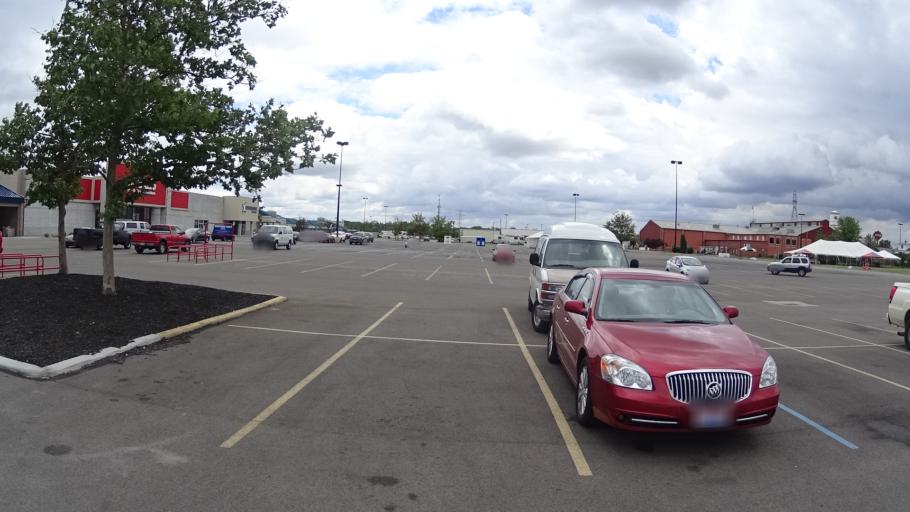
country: US
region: Ohio
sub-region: Erie County
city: Sandusky
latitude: 41.4066
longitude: -82.6598
